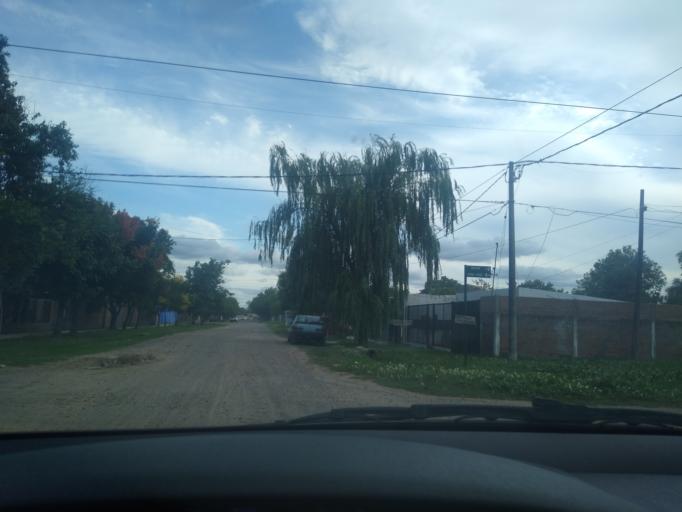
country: AR
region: Chaco
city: Resistencia
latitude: -27.4828
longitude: -58.9755
